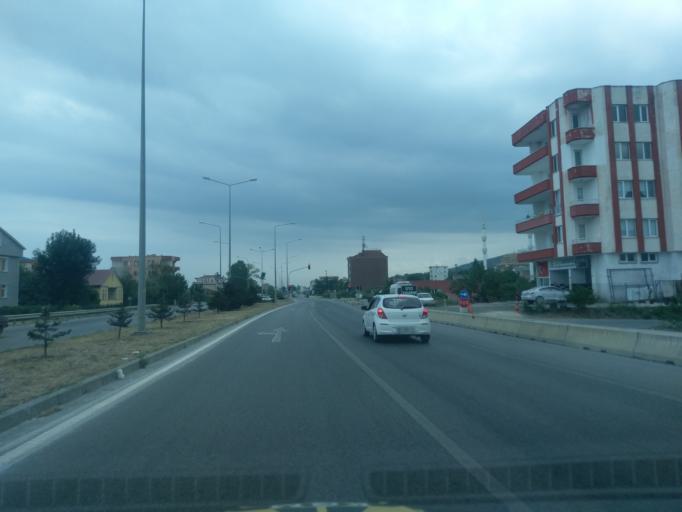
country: TR
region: Samsun
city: Taflan
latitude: 41.4045
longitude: 36.1844
